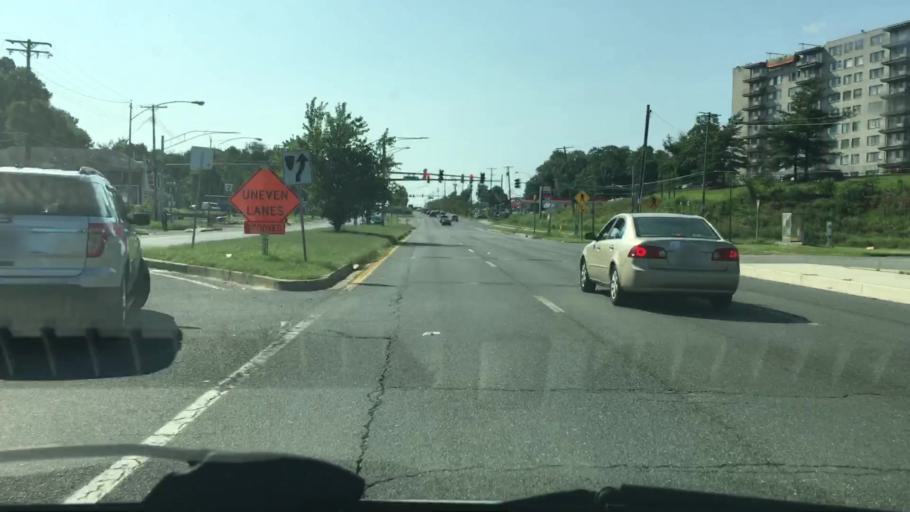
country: US
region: Maryland
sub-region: Prince George's County
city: Silver Hill
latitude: 38.8491
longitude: -76.9539
